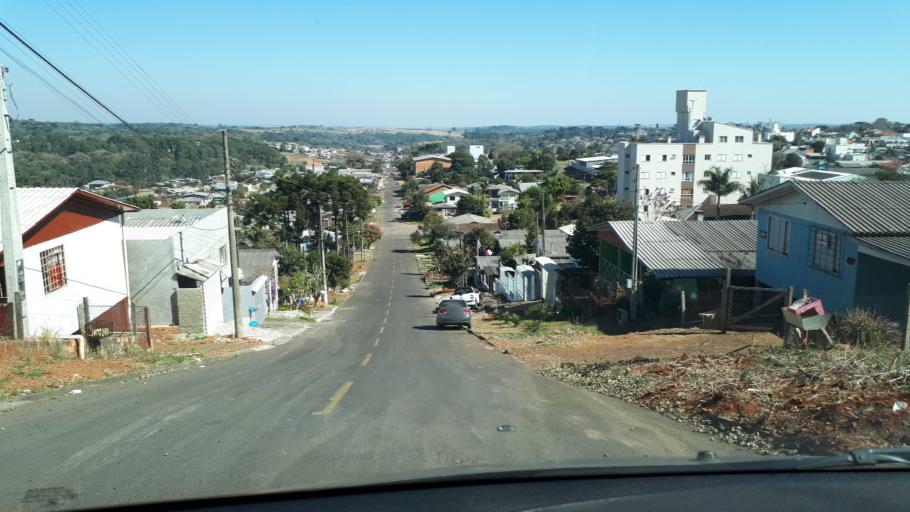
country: BR
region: Santa Catarina
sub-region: Chapeco
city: Chapeco
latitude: -27.1242
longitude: -52.6070
